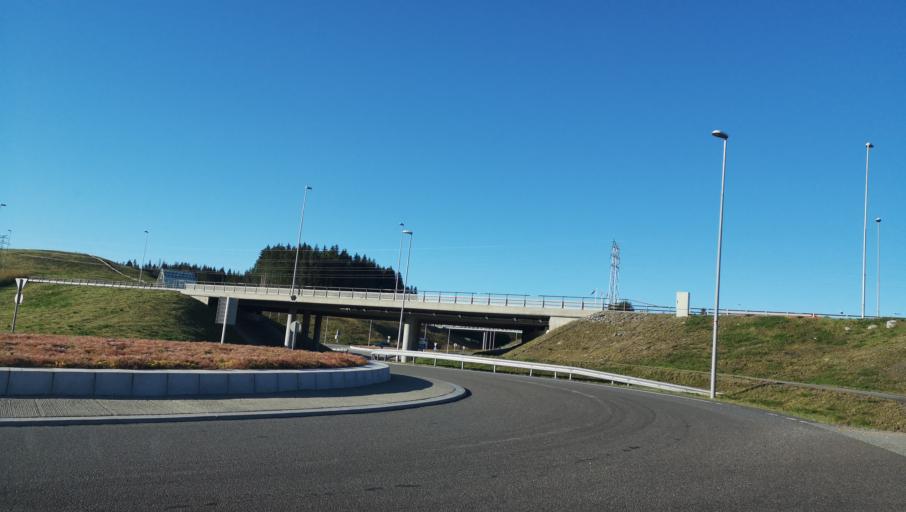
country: NO
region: Ostfold
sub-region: Hobol
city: Knappstad
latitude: 59.6196
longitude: 11.0056
